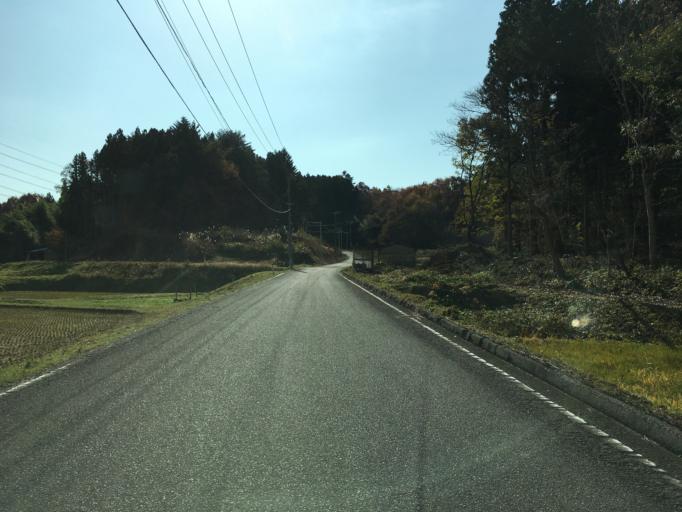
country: JP
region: Fukushima
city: Ishikawa
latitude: 37.1686
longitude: 140.5567
